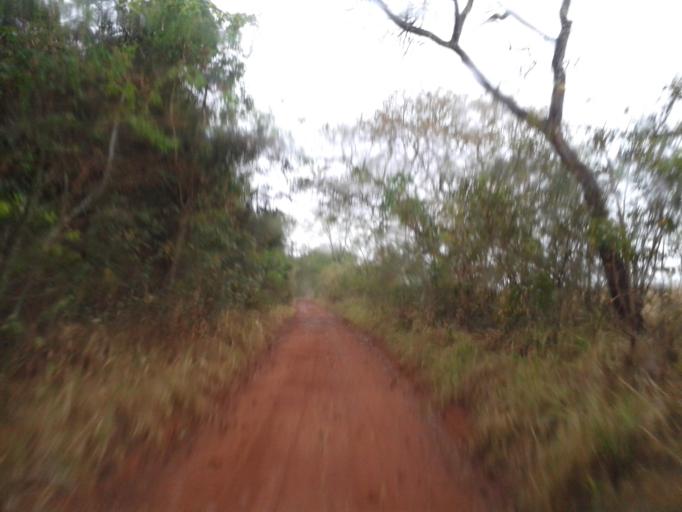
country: BR
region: Minas Gerais
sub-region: Campina Verde
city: Campina Verde
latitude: -19.3496
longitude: -49.5313
